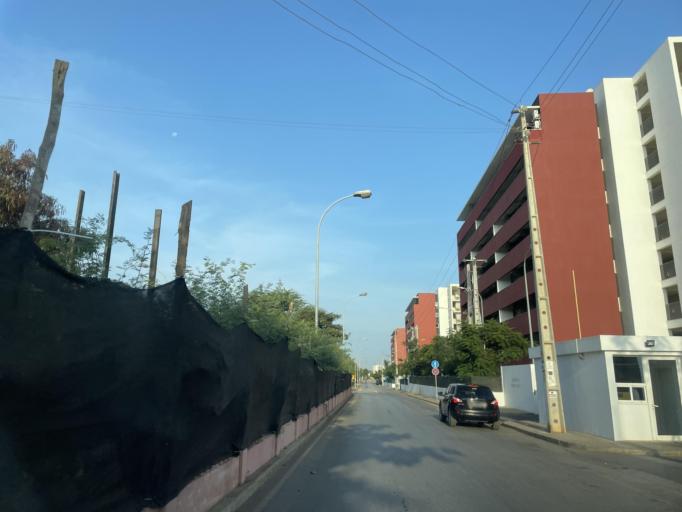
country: AO
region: Luanda
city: Luanda
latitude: -8.9105
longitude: 13.1846
